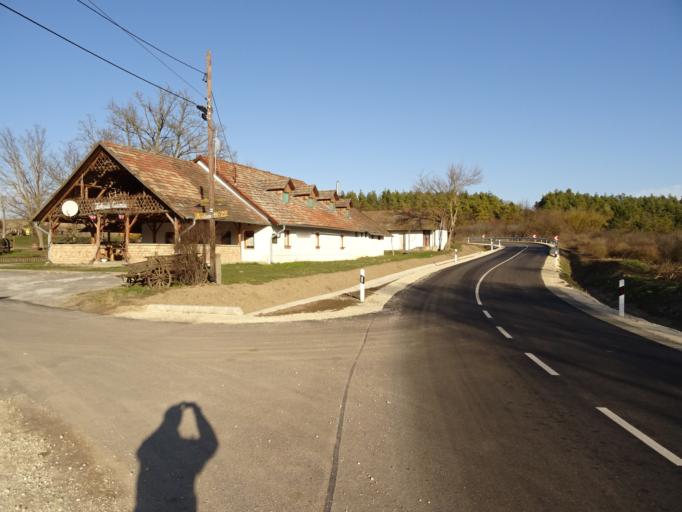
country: HU
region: Pest
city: Uri
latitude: 47.3934
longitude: 19.5129
